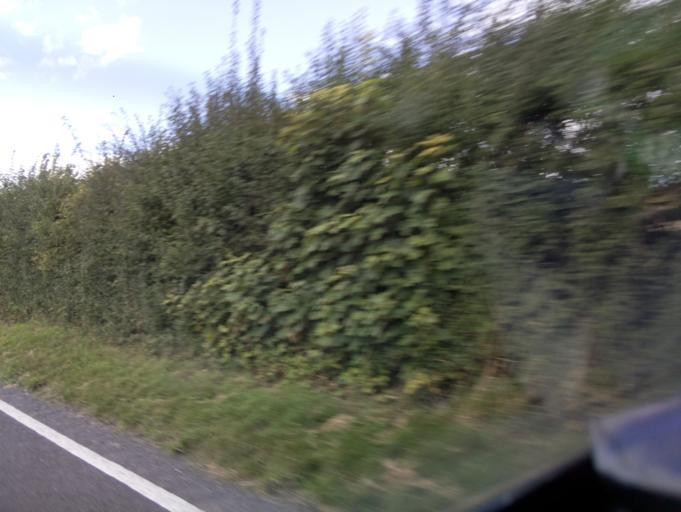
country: GB
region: England
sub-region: Hampshire
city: Chandlers Ford
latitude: 51.1057
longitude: -1.4176
